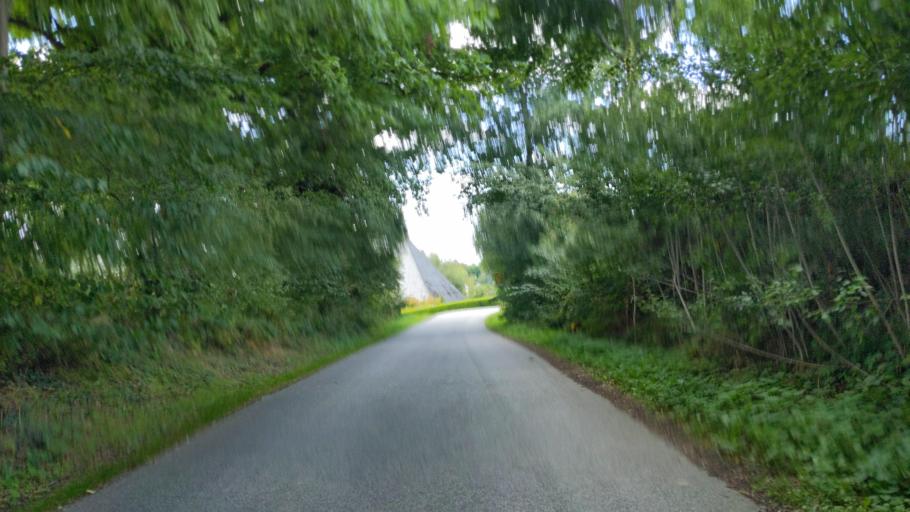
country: DE
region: Schleswig-Holstein
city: Kasseedorf
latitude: 54.1205
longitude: 10.7129
